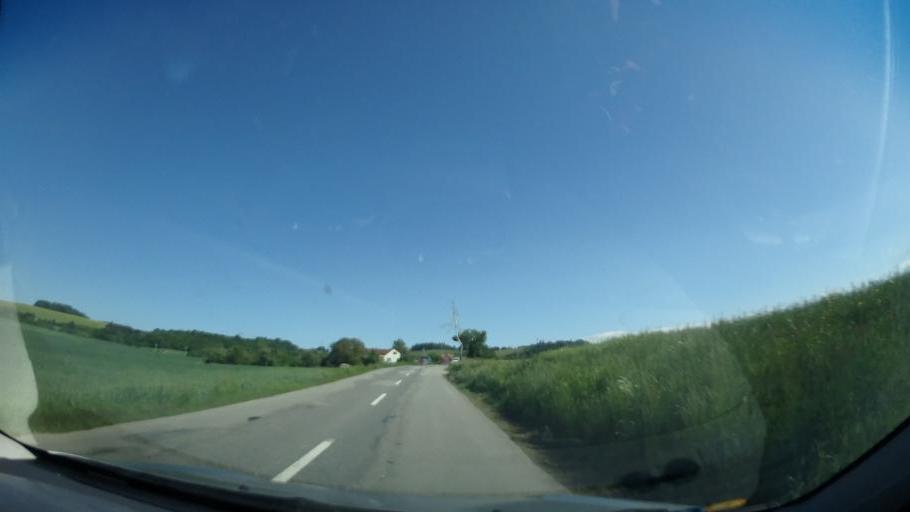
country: CZ
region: South Moravian
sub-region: Okres Blansko
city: Letovice
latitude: 49.5895
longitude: 16.5954
